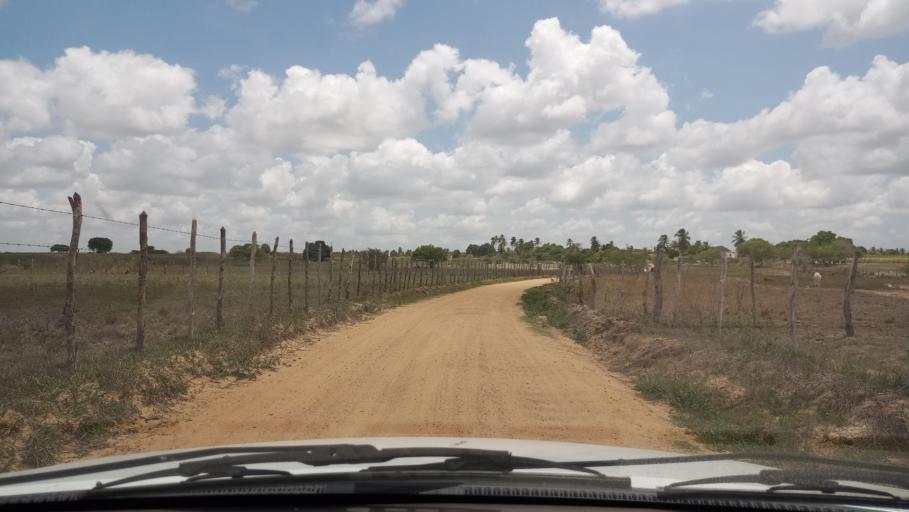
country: BR
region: Rio Grande do Norte
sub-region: Brejinho
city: Brejinho
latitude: -6.2938
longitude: -35.3506
